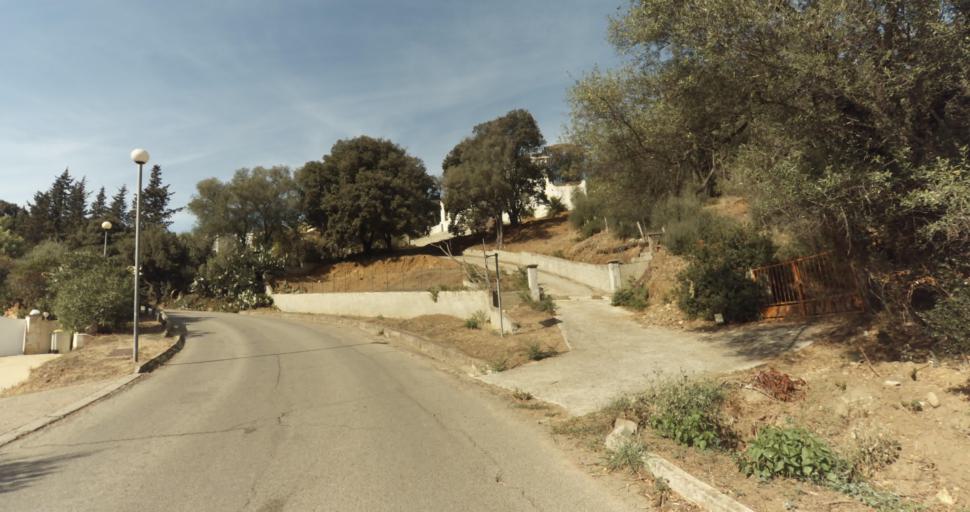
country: FR
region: Corsica
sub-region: Departement de la Corse-du-Sud
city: Ajaccio
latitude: 41.9327
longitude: 8.7256
